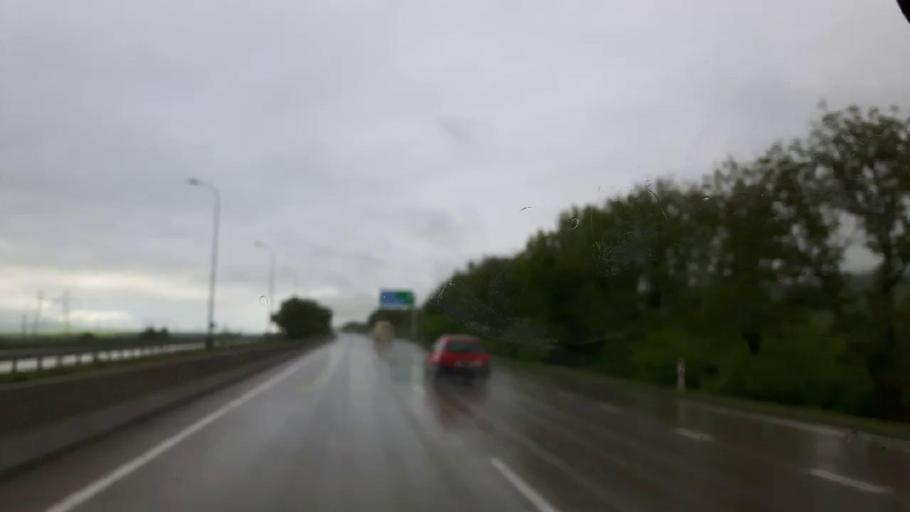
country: GE
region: Shida Kartli
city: Kaspi
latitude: 42.0142
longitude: 44.3253
